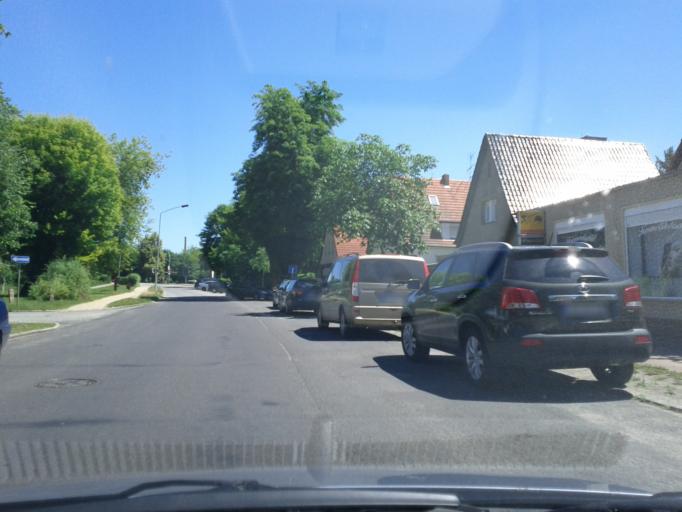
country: DE
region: Brandenburg
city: Furstenwalde
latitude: 52.3538
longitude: 14.0600
